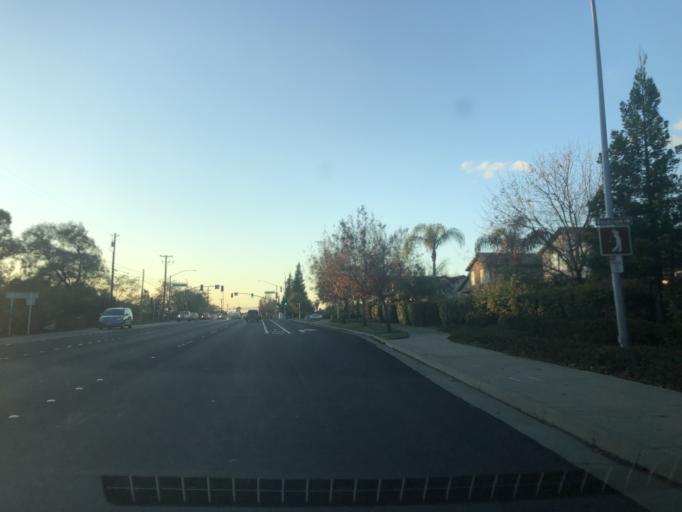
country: US
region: California
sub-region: Sacramento County
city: Antelope
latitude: 38.7519
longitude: -121.3352
